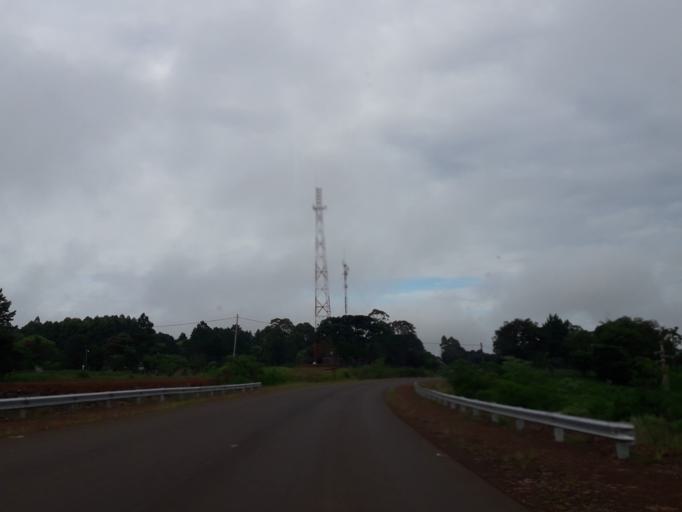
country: AR
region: Misiones
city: Bernardo de Irigoyen
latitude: -26.4245
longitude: -53.8404
